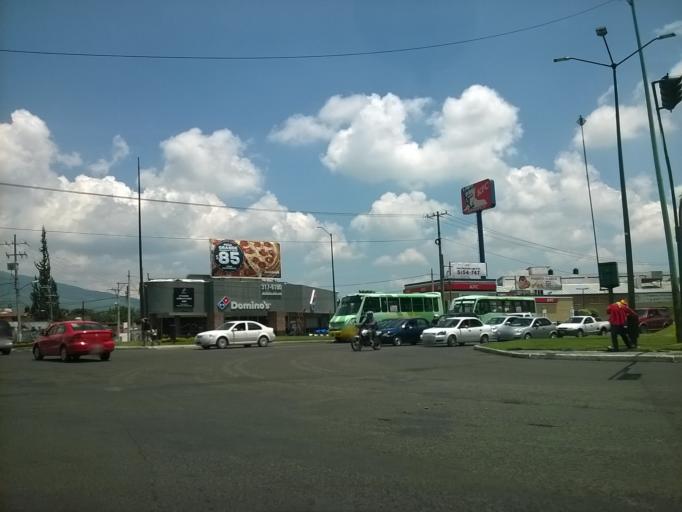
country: MX
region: Michoacan
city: Morelia
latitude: 19.7107
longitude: -101.1885
